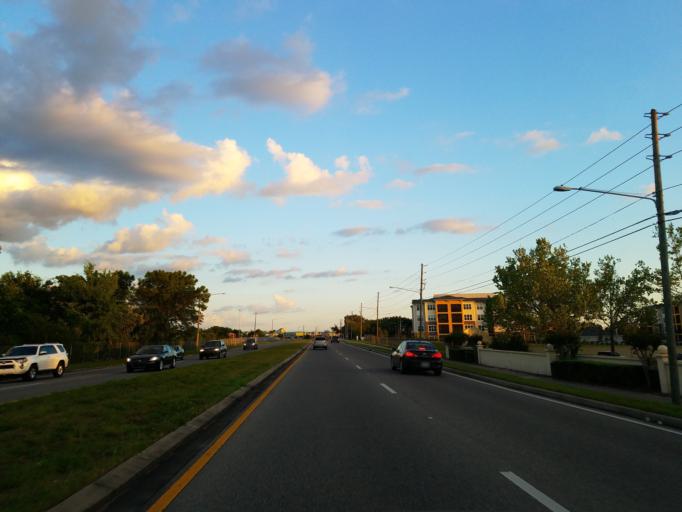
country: US
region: Florida
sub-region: Orange County
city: Williamsburg
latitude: 28.4184
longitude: -81.4758
